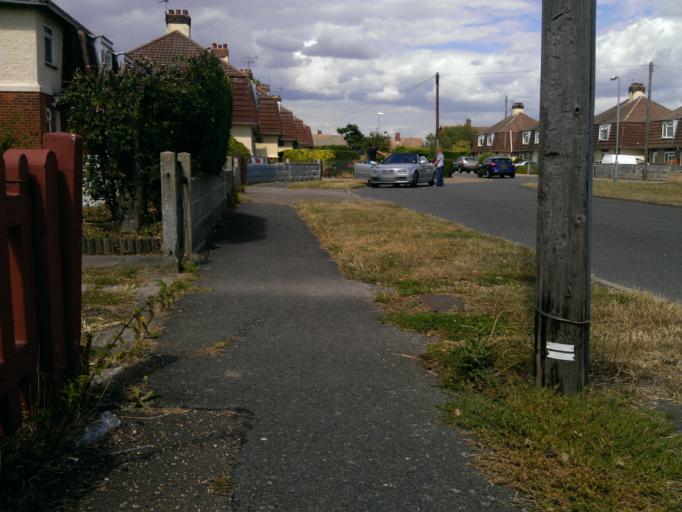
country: GB
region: England
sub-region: Essex
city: Clacton-on-Sea
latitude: 51.8063
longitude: 1.1535
